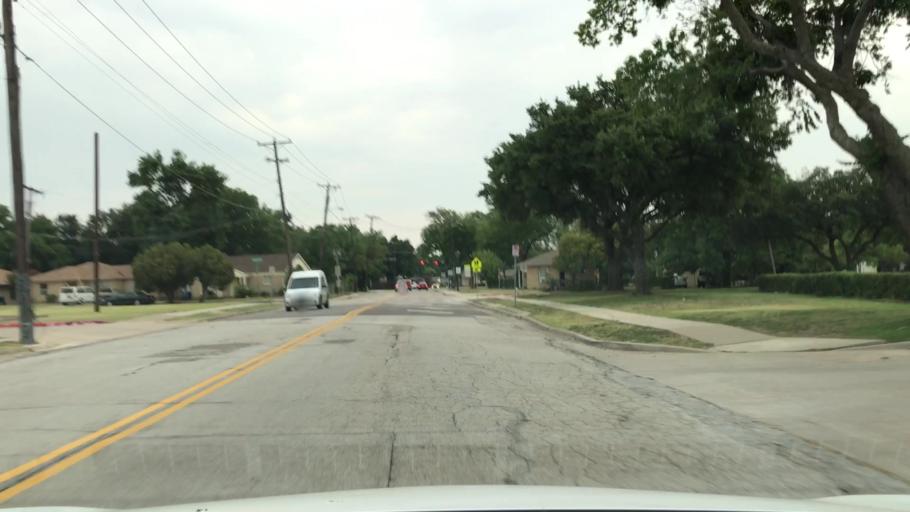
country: US
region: Texas
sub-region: Dallas County
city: Carrollton
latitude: 32.9553
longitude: -96.8950
